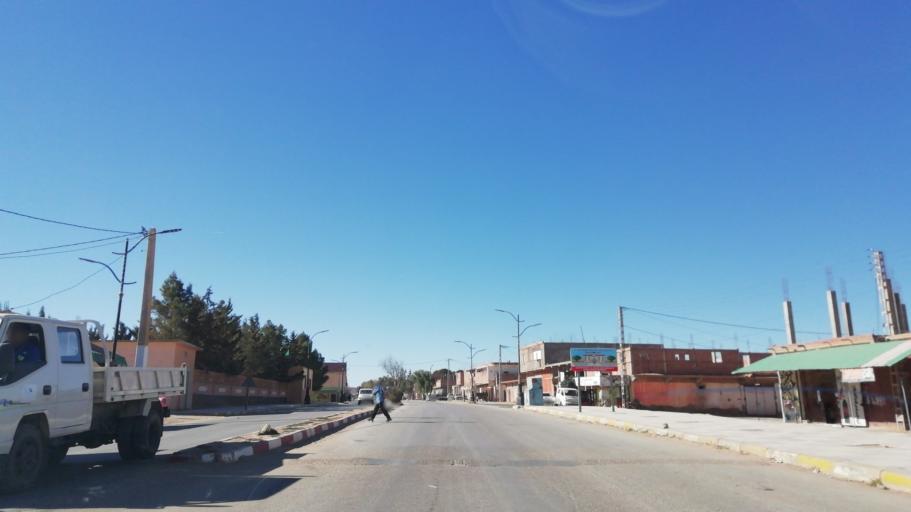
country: DZ
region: El Bayadh
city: El Bayadh
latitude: 33.7279
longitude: 1.5373
